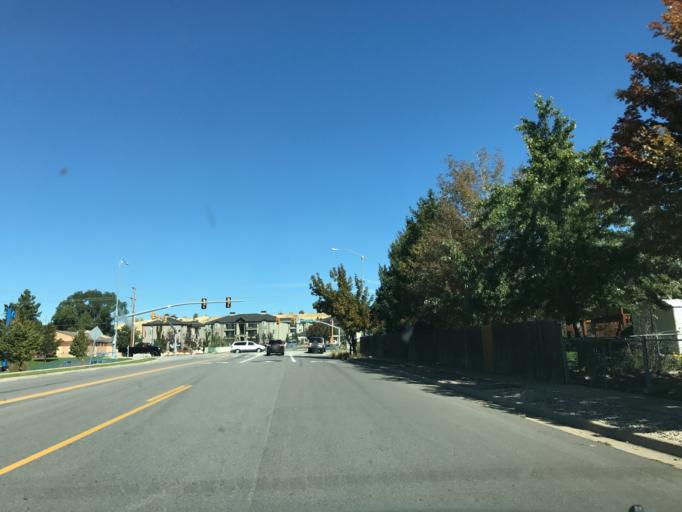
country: US
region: Utah
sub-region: Davis County
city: South Weber
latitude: 41.1004
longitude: -111.9391
